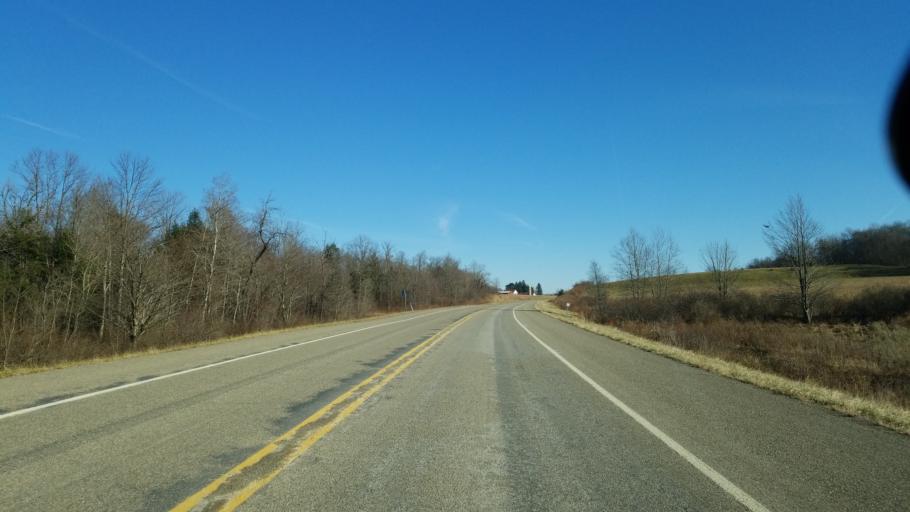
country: US
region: Pennsylvania
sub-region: Jefferson County
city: Reynoldsville
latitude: 41.1884
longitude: -78.8906
